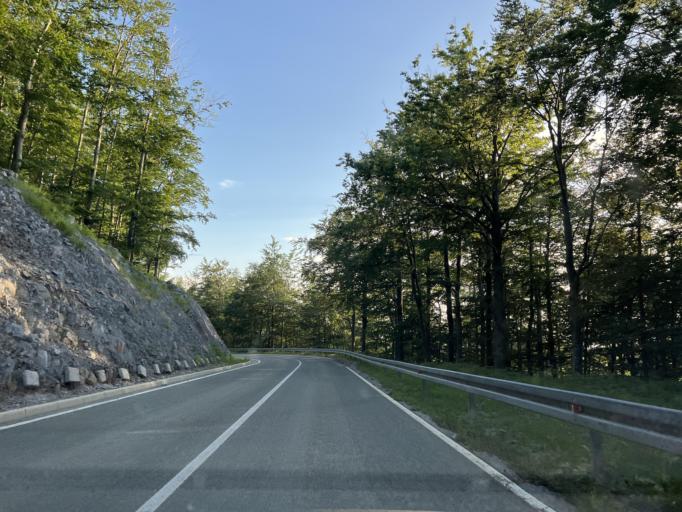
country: HR
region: Primorsko-Goranska
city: Podhum
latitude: 45.4155
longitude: 14.5643
